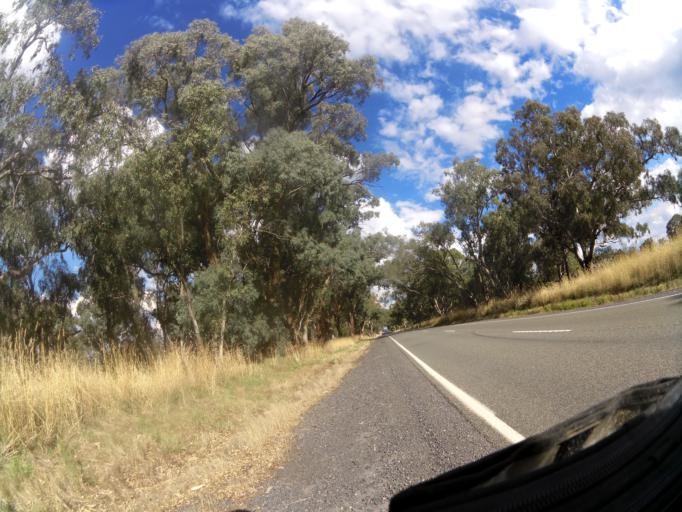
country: AU
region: Victoria
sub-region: Mansfield
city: Mansfield
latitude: -37.0107
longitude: 146.0846
